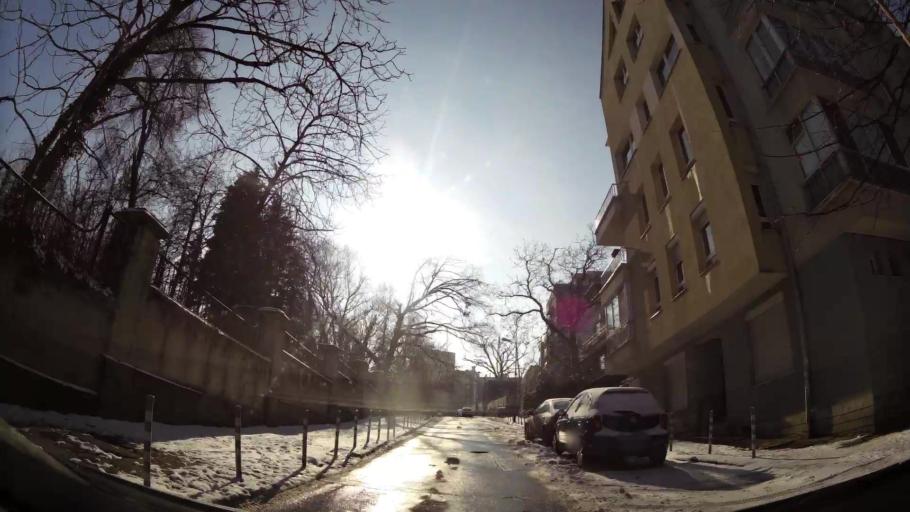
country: BG
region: Sofia-Capital
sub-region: Stolichna Obshtina
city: Sofia
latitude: 42.6751
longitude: 23.3253
